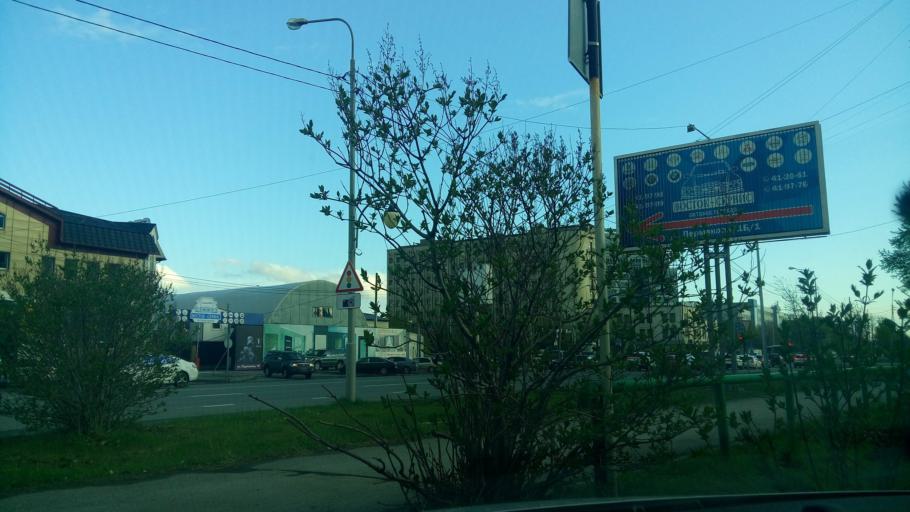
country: RU
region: Tjumen
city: Melioratorov
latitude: 57.1351
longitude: 65.6049
